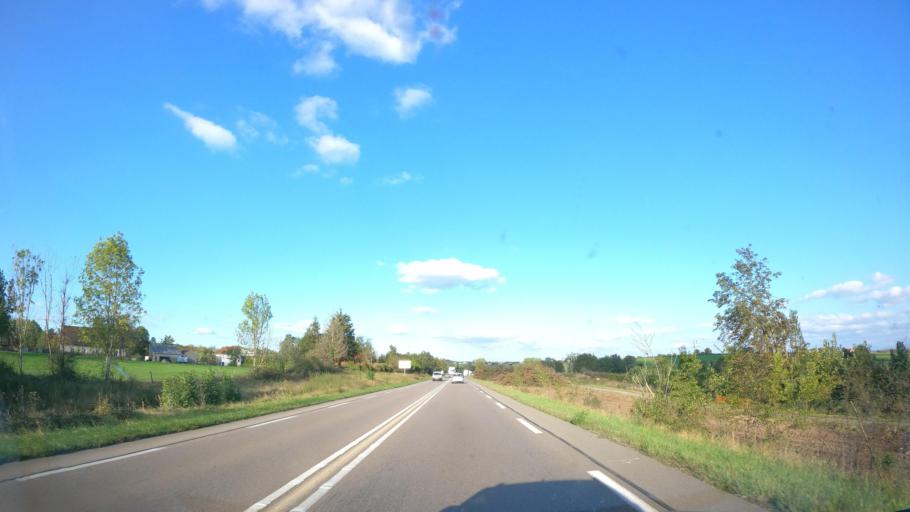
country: FR
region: Bourgogne
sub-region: Departement de Saone-et-Loire
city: Ciry-le-Noble
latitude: 46.6141
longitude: 4.2716
